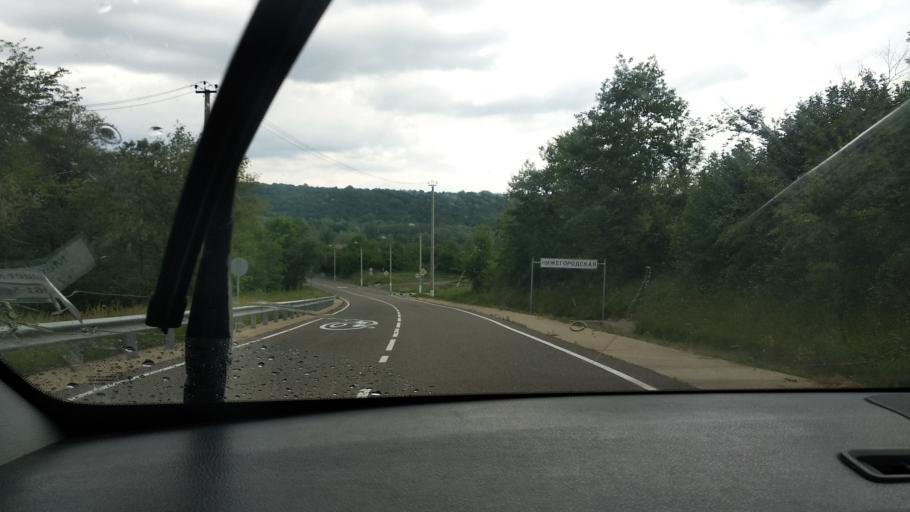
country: RU
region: Krasnodarskiy
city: Neftegorsk
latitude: 44.2730
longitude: 39.9274
